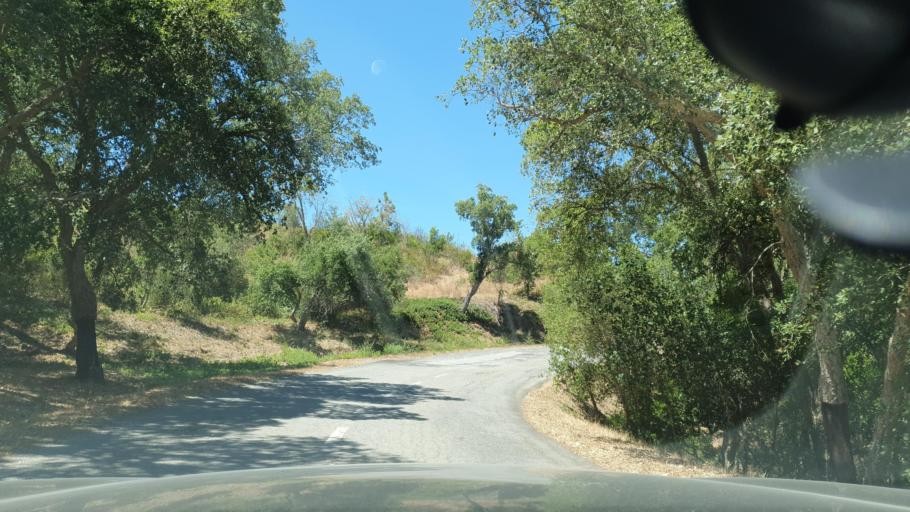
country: PT
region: Beja
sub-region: Odemira
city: Odemira
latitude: 37.6053
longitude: -8.4949
